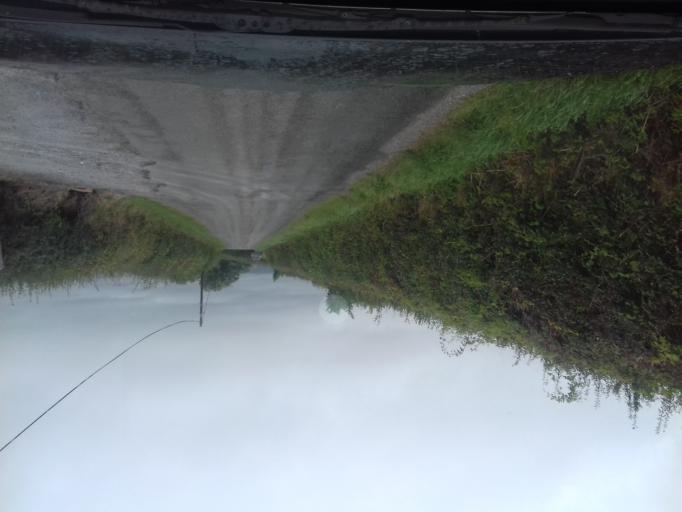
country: IE
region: Leinster
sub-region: Kilkenny
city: Graiguenamanagh
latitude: 52.5965
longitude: -7.0107
